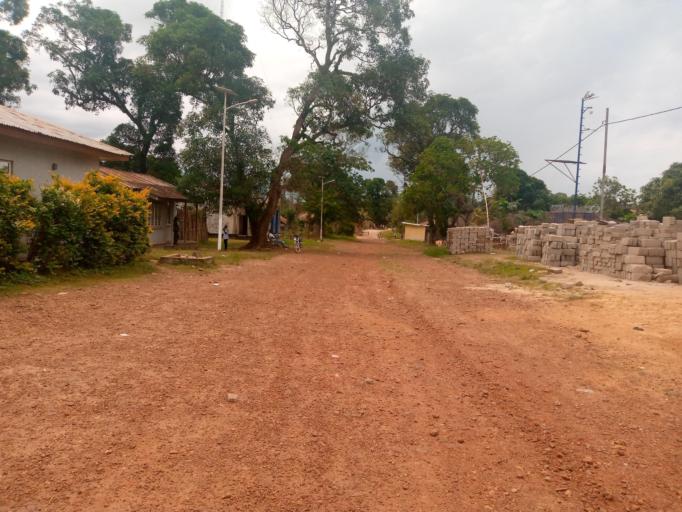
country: SL
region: Southern Province
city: Mogbwemo
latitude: 7.6066
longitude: -12.1764
